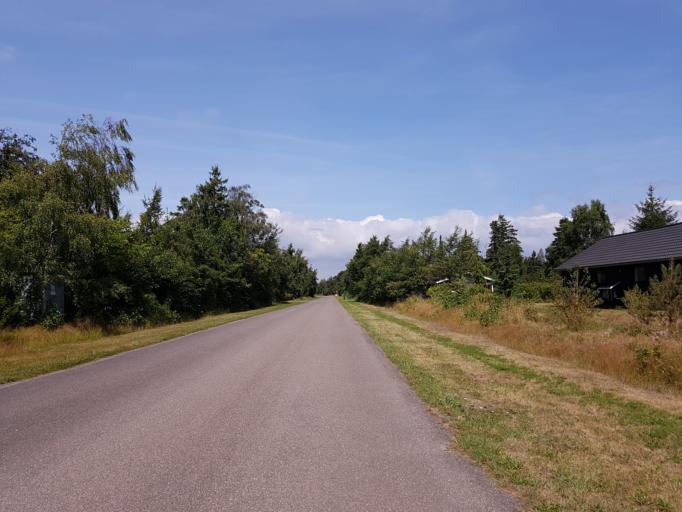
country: DK
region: Zealand
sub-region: Guldborgsund Kommune
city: Nykobing Falster
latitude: 54.5942
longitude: 11.9652
